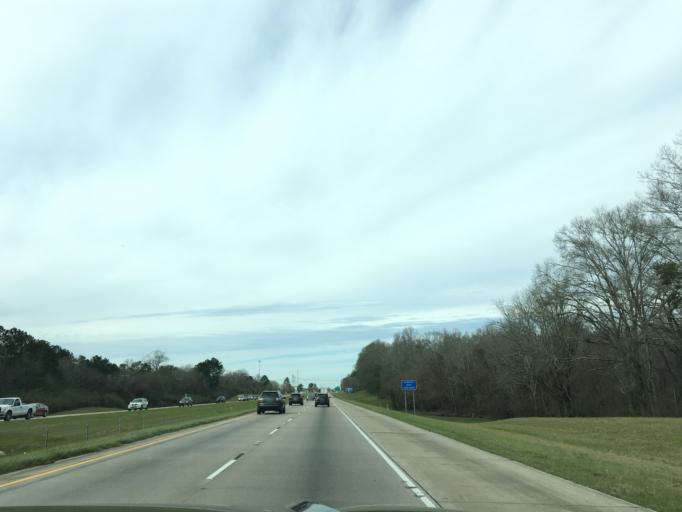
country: US
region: Louisiana
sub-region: East Baton Rouge Parish
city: Old Jefferson
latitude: 30.3339
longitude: -91.0176
